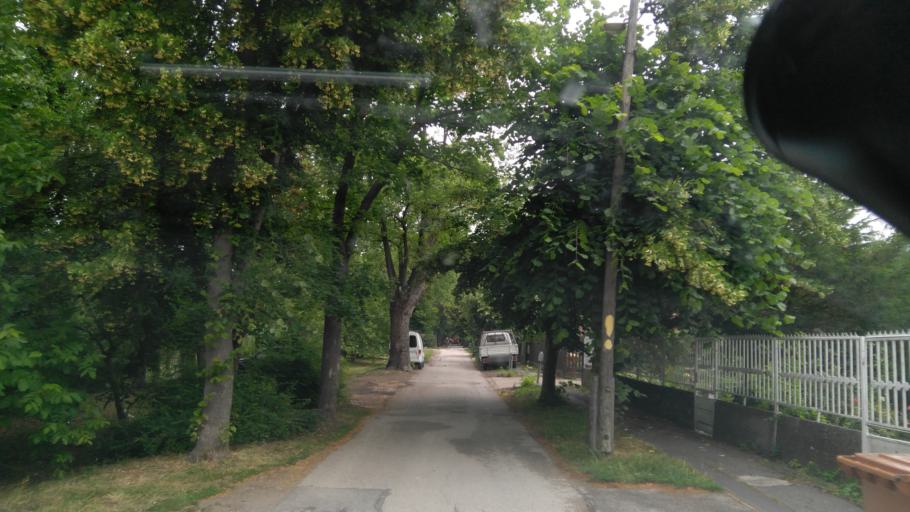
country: HU
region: Bekes
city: Bekescsaba
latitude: 46.6876
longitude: 21.0994
